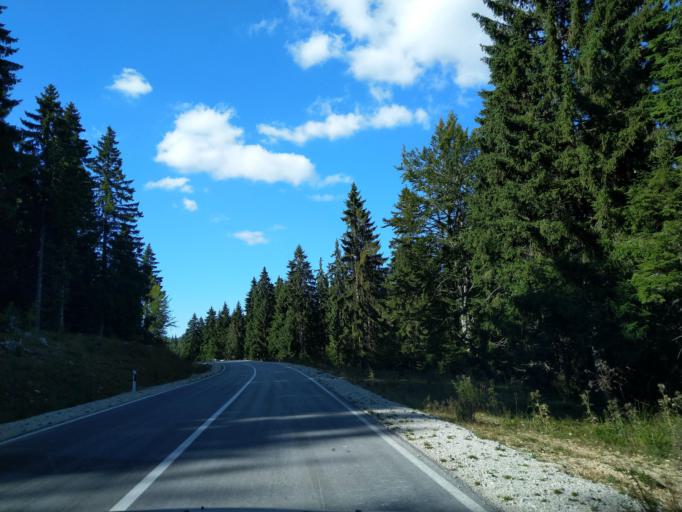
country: RS
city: Sokolovica
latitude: 43.2940
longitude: 20.3095
